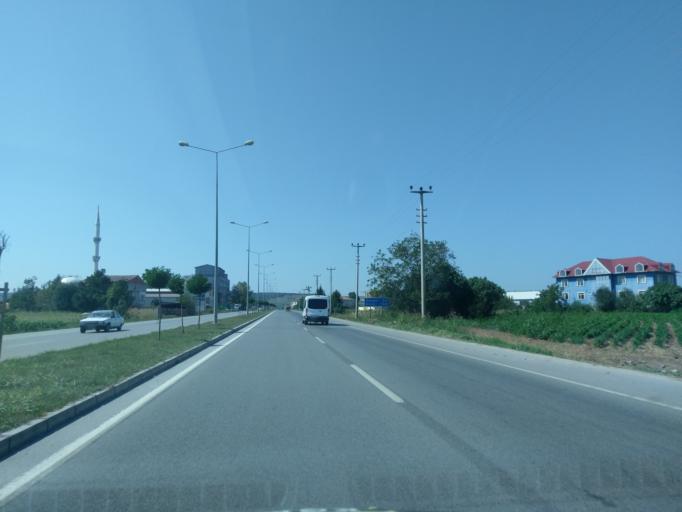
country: TR
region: Samsun
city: Bafra
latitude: 41.5726
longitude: 35.8692
